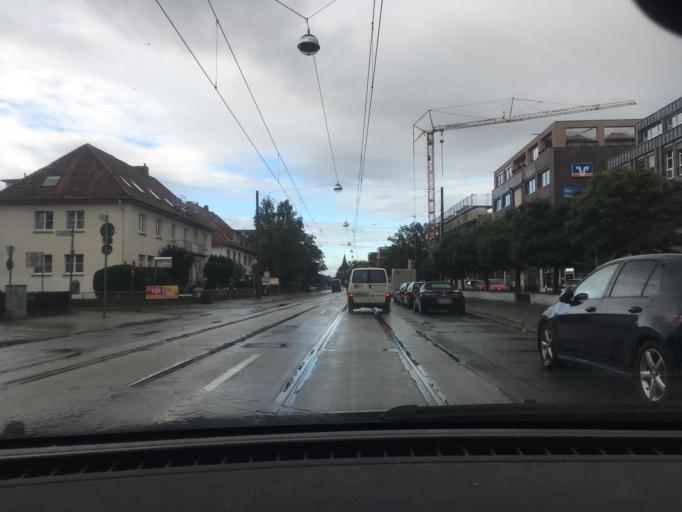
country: DE
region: Lower Saxony
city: Langenhagen
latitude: 52.4087
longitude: 9.7997
